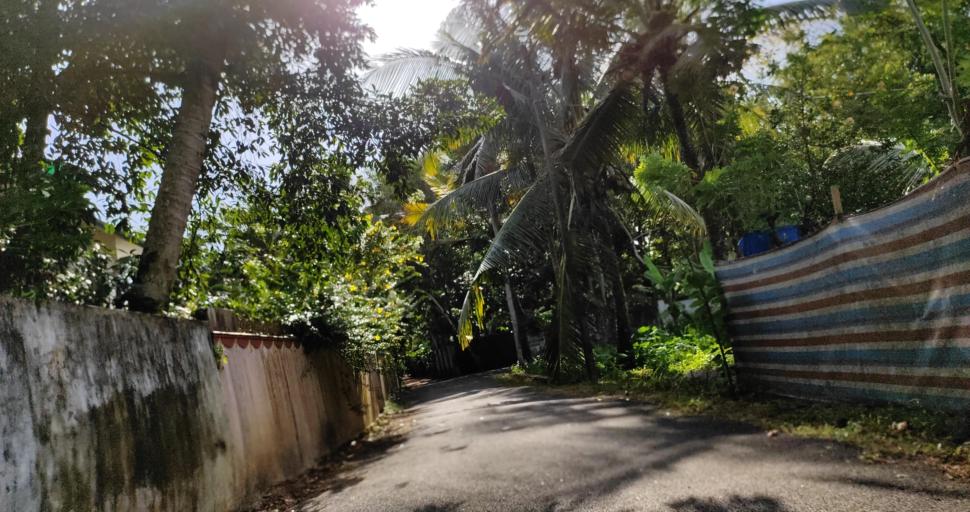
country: IN
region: Kerala
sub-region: Alappuzha
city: Shertallai
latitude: 9.6024
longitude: 76.3312
